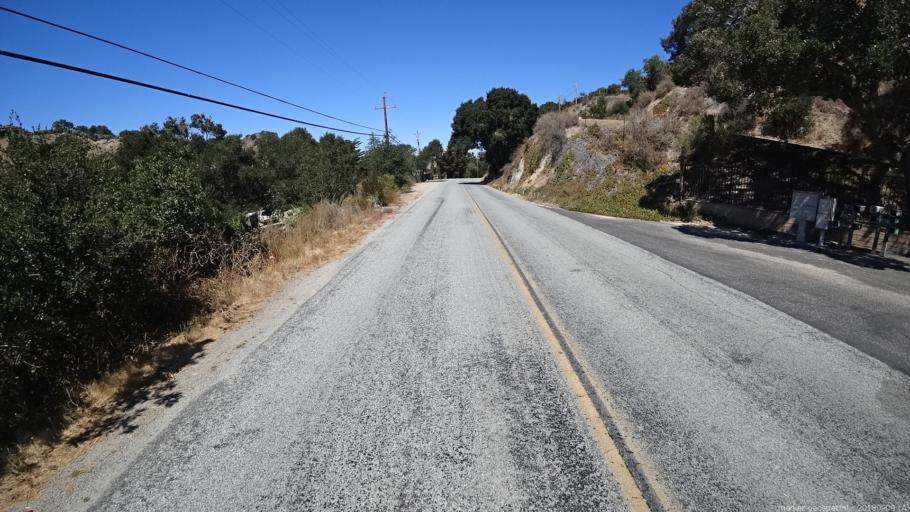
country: US
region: California
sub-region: Monterey County
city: Carmel Valley Village
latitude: 36.5606
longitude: -121.7001
